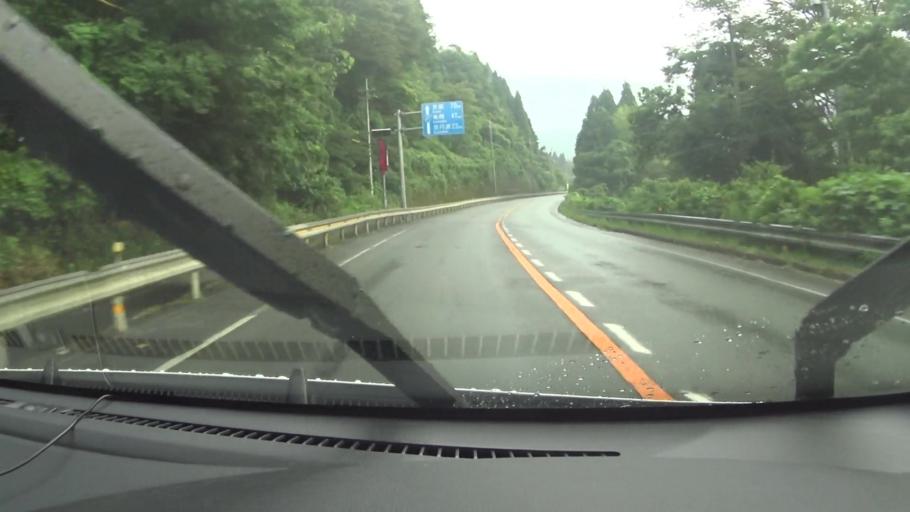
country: JP
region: Kyoto
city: Ayabe
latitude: 35.2856
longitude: 135.3358
